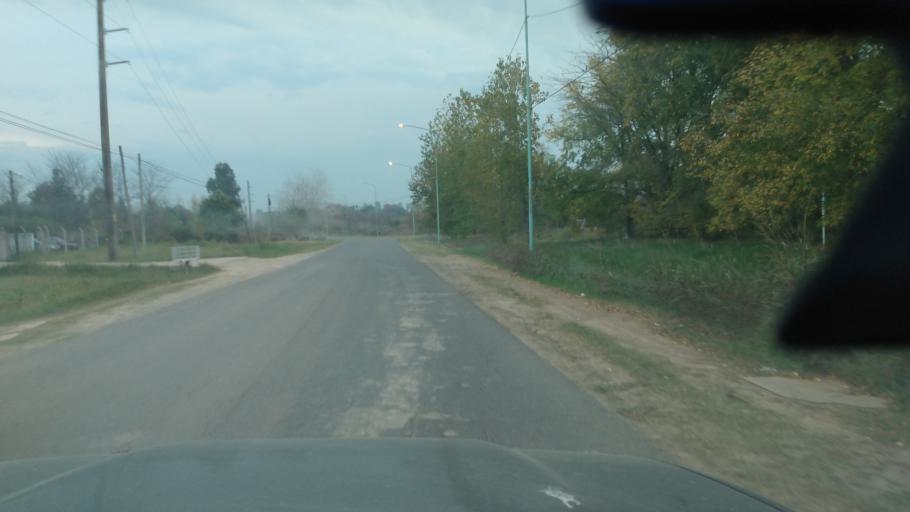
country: AR
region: Buenos Aires
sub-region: Partido de Lujan
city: Lujan
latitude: -34.5660
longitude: -59.1445
